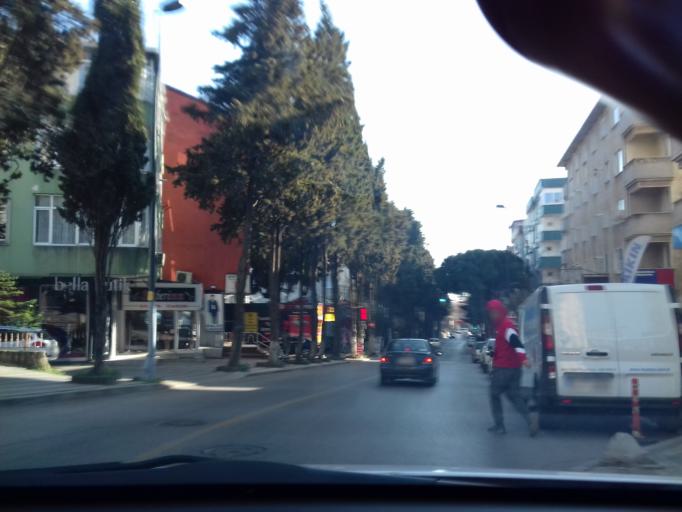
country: TR
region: Istanbul
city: Umraniye
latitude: 41.0211
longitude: 29.0816
